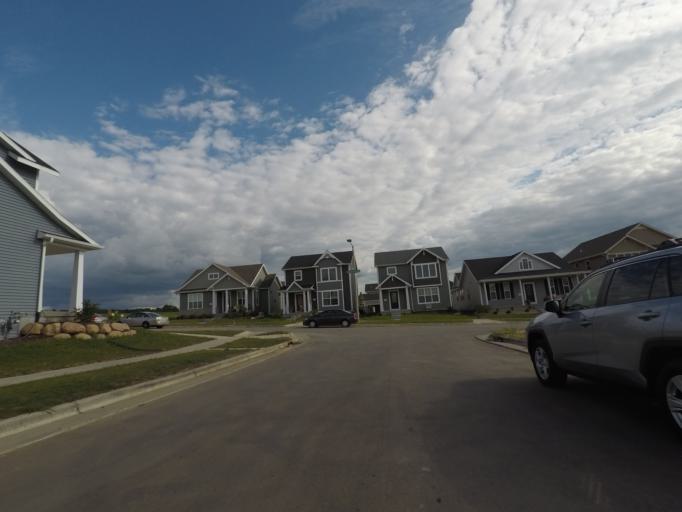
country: US
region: Wisconsin
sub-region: Dane County
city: Verona
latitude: 43.0522
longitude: -89.5488
